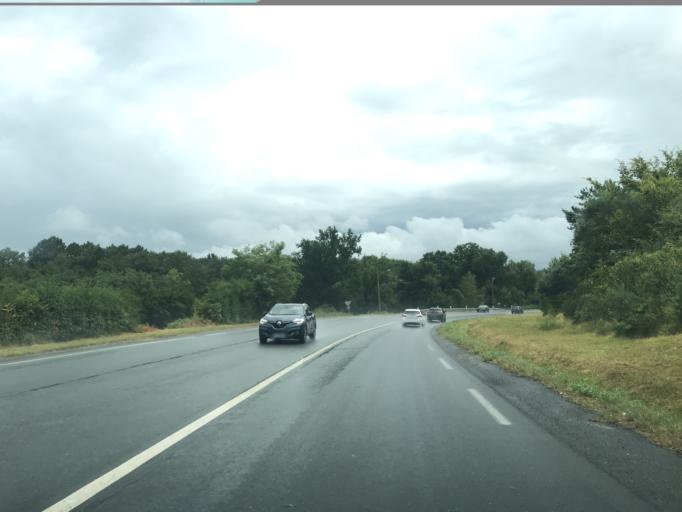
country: FR
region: Aquitaine
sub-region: Departement de la Dordogne
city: Coulounieix-Chamiers
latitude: 45.1503
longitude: 0.7032
